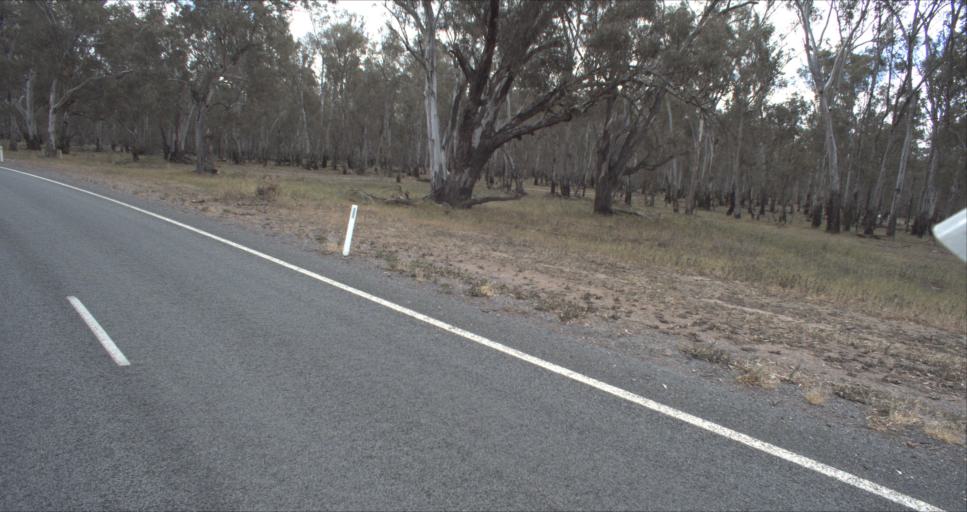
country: AU
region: New South Wales
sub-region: Leeton
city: Leeton
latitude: -34.6410
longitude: 146.3598
